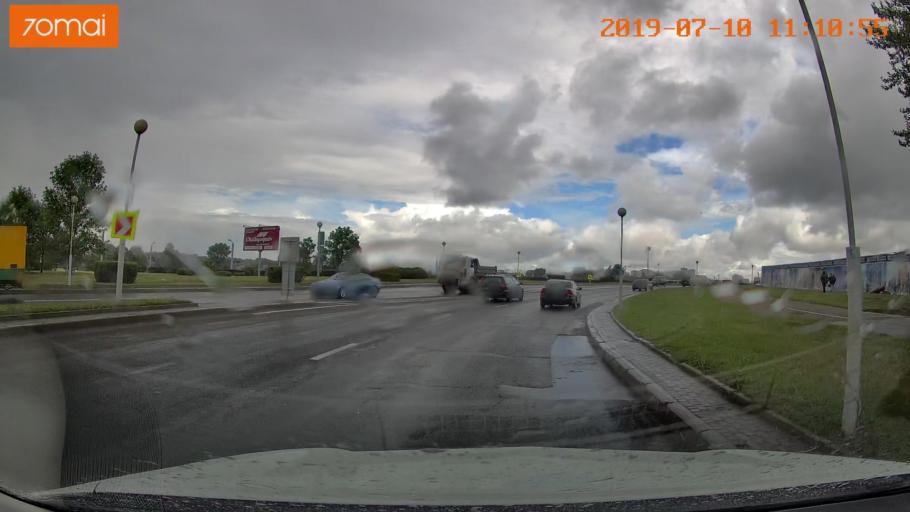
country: BY
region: Minsk
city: Syenitsa
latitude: 53.8695
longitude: 27.5237
